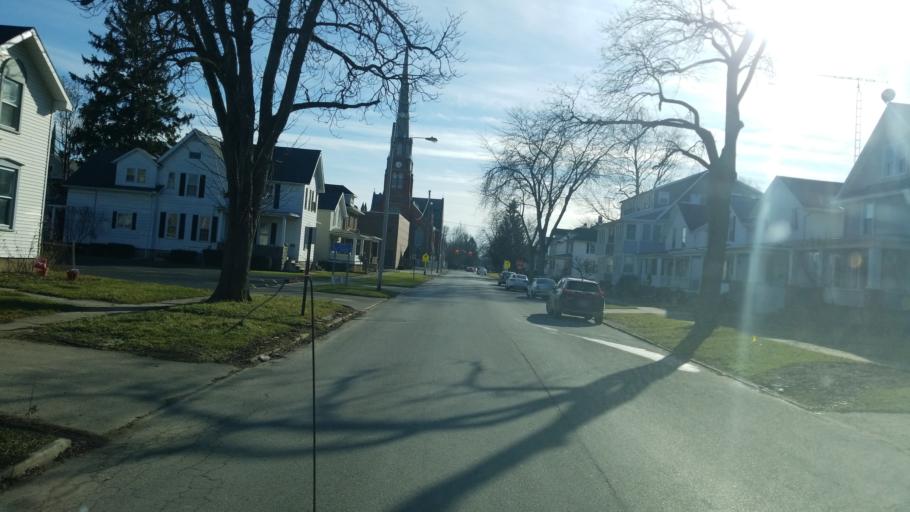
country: US
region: Ohio
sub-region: Sandusky County
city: Fremont
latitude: 41.3484
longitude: -83.1197
